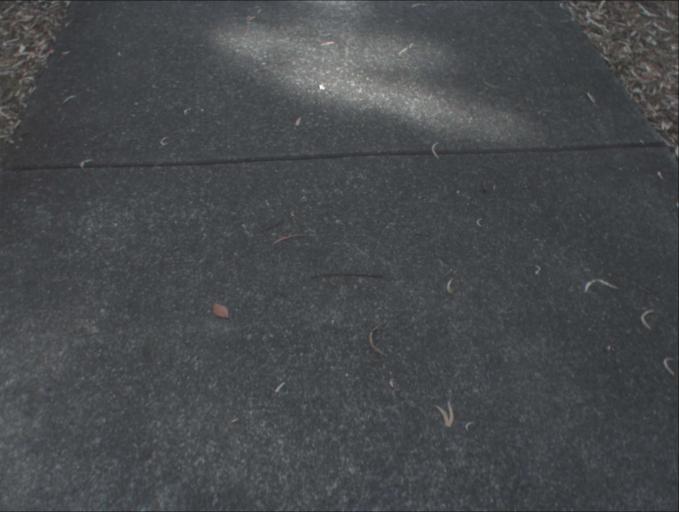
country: AU
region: Queensland
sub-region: Logan
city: Beenleigh
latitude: -27.7046
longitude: 153.1966
